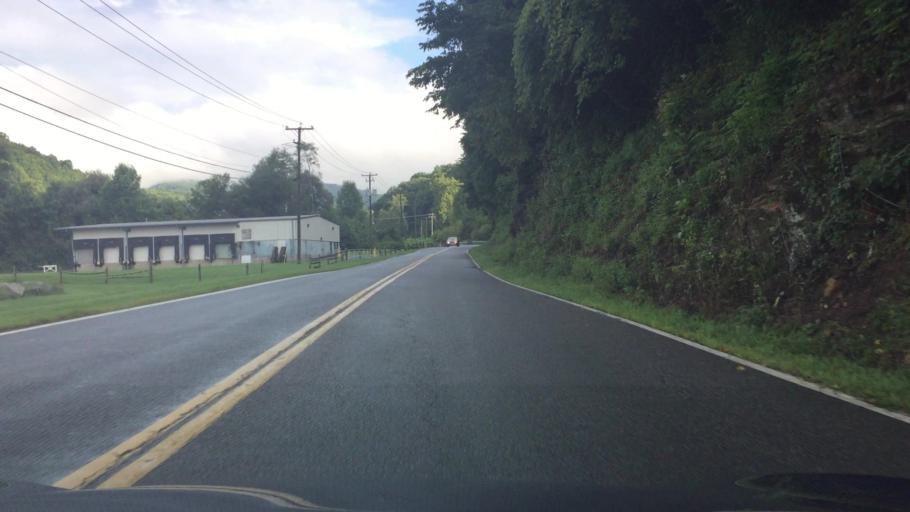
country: US
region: Virginia
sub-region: Smyth County
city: Atkins
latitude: 36.8597
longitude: -81.4322
